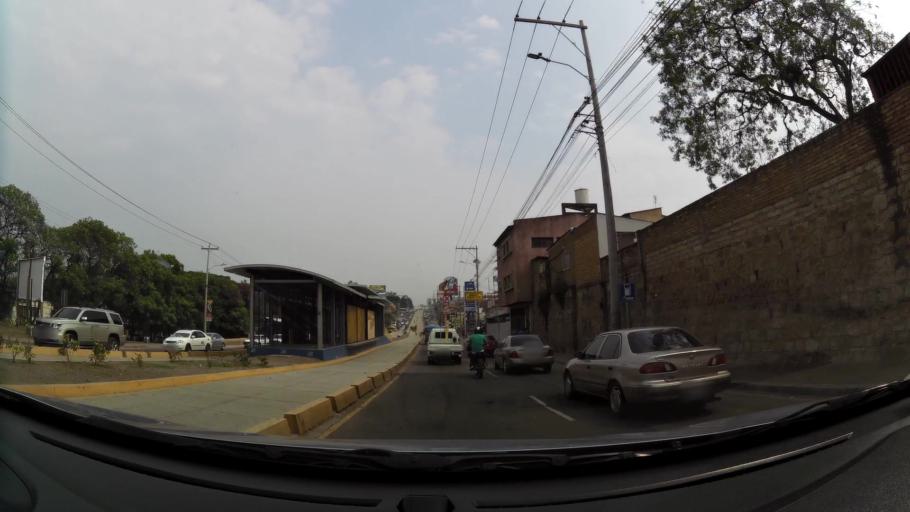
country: HN
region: Francisco Morazan
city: Tegucigalpa
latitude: 14.0731
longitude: -87.1848
